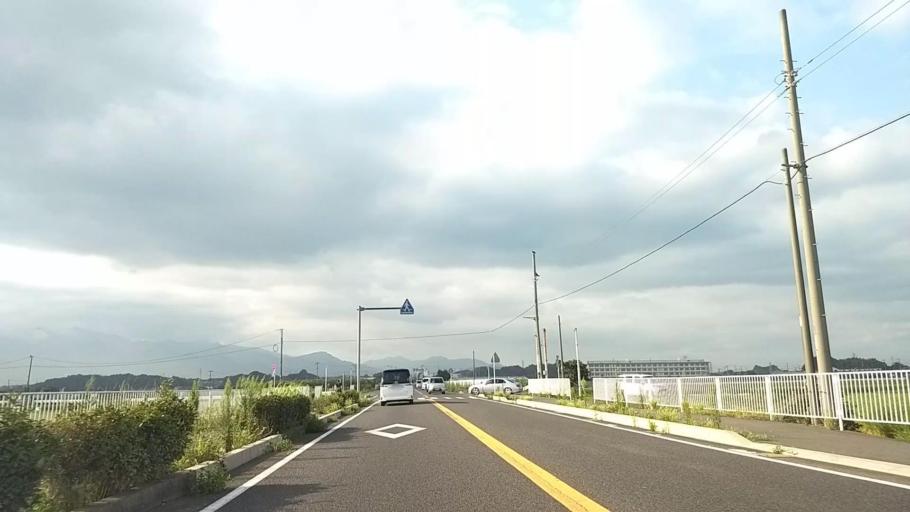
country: JP
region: Kanagawa
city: Isehara
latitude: 35.3659
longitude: 139.3233
